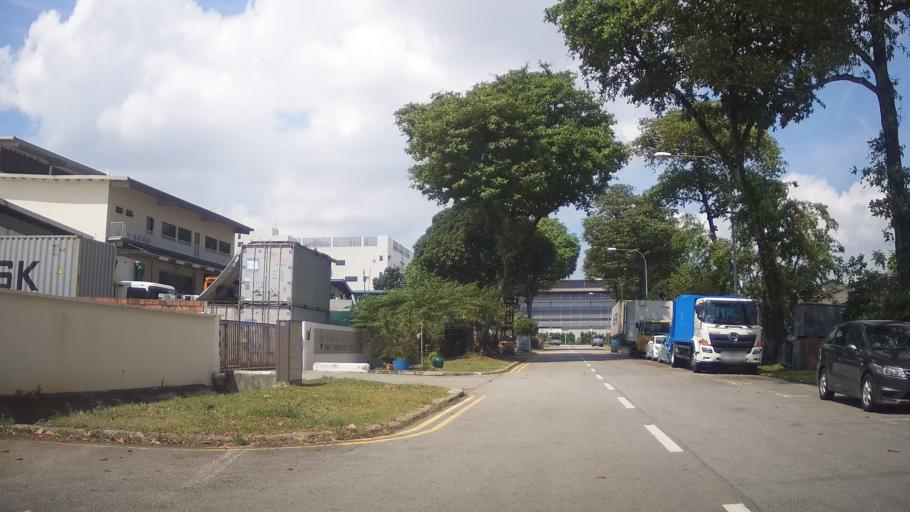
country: SG
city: Singapore
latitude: 1.3278
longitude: 103.7121
